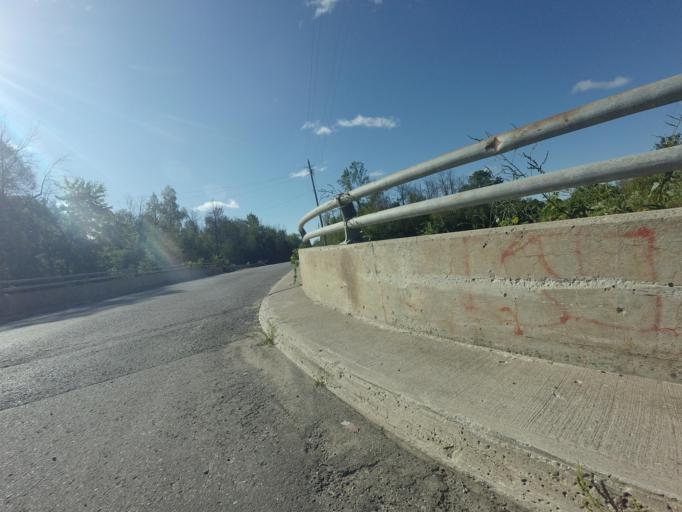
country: CA
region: Ontario
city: Bradford West Gwillimbury
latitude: 44.0551
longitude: -79.5594
